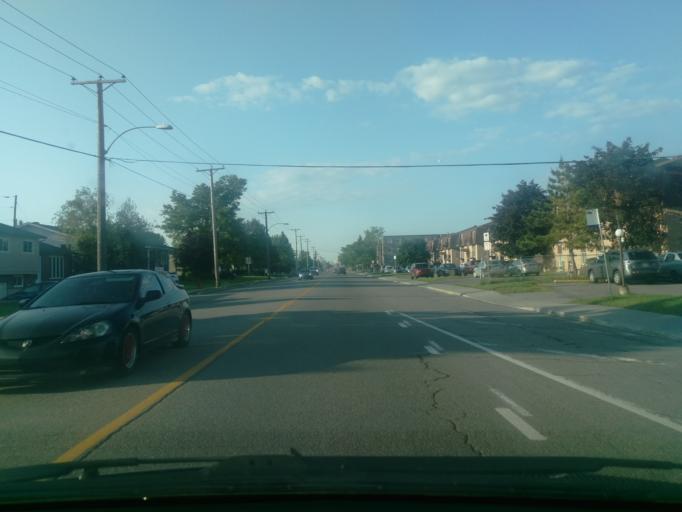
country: CA
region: Quebec
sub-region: Outaouais
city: Gatineau
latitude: 45.4857
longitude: -75.7021
